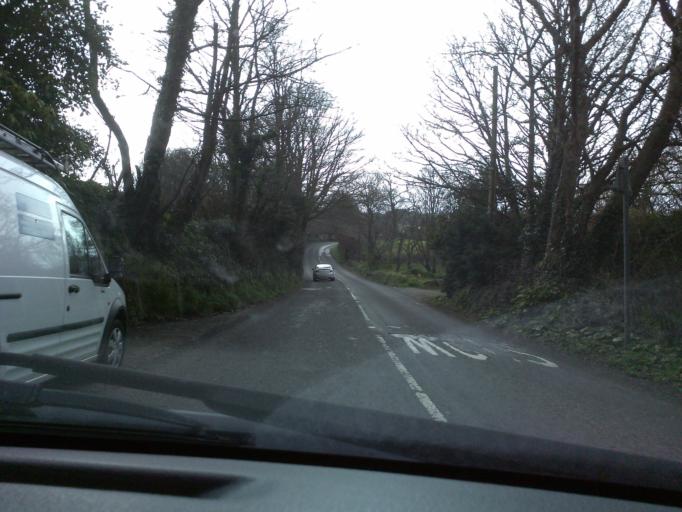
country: GB
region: England
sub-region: Cornwall
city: Penzance
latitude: 50.1037
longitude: -5.5779
